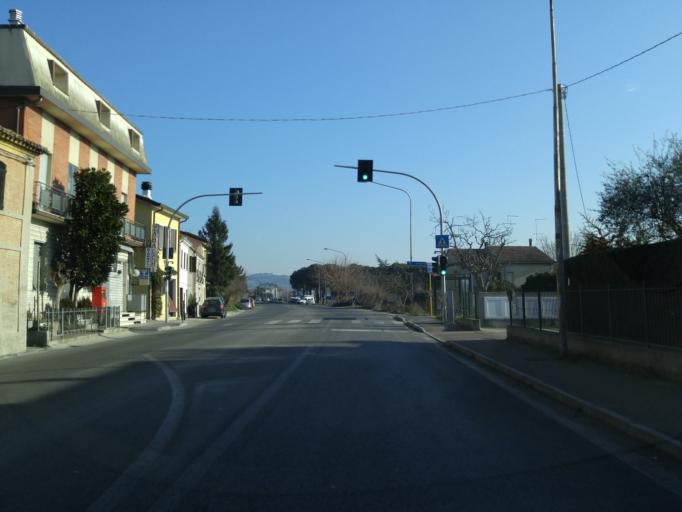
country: IT
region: The Marches
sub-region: Provincia di Pesaro e Urbino
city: Gabicce Mare
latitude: 43.9557
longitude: 12.7679
